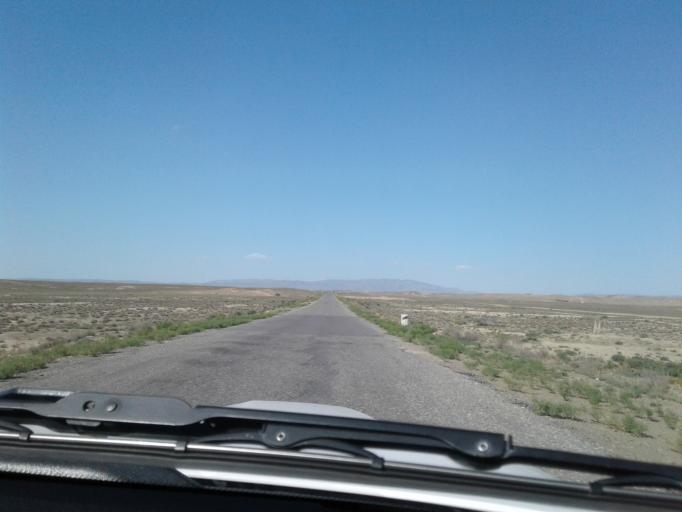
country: TM
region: Balkan
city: Magtymguly
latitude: 38.6196
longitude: 56.2277
